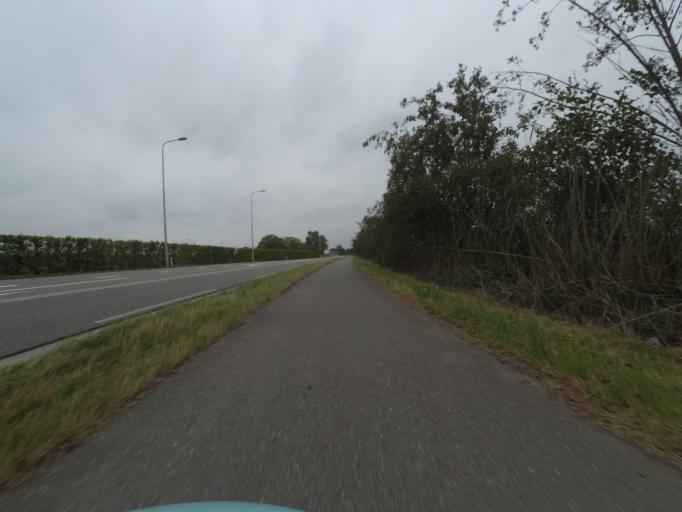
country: NL
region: Utrecht
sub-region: Gemeente Wijk bij Duurstede
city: Wijk bij Duurstede
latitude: 51.9076
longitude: 5.3611
